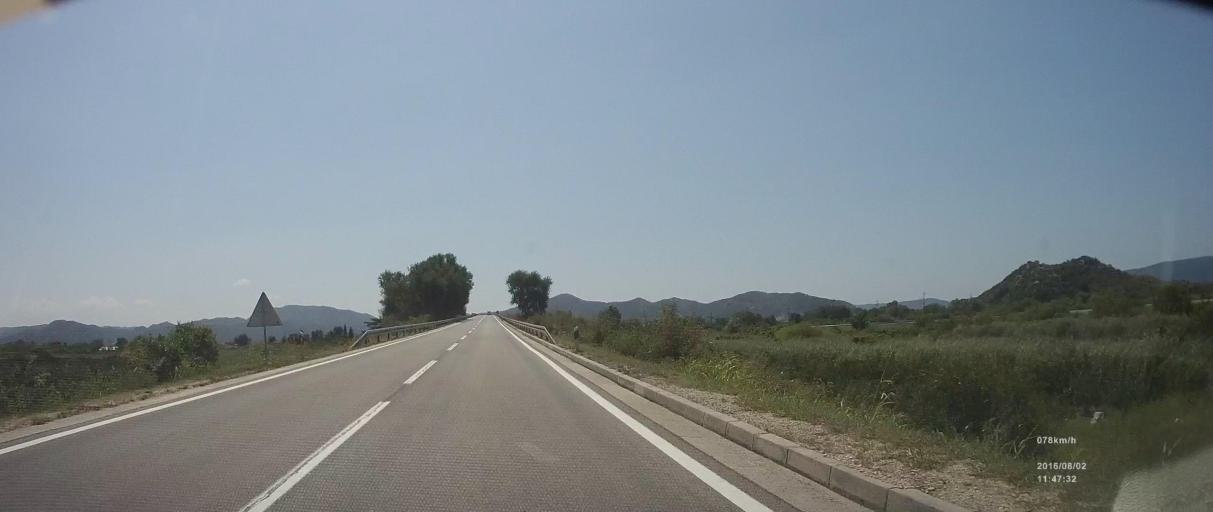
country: HR
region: Dubrovacko-Neretvanska
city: Komin
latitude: 43.0428
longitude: 17.4827
